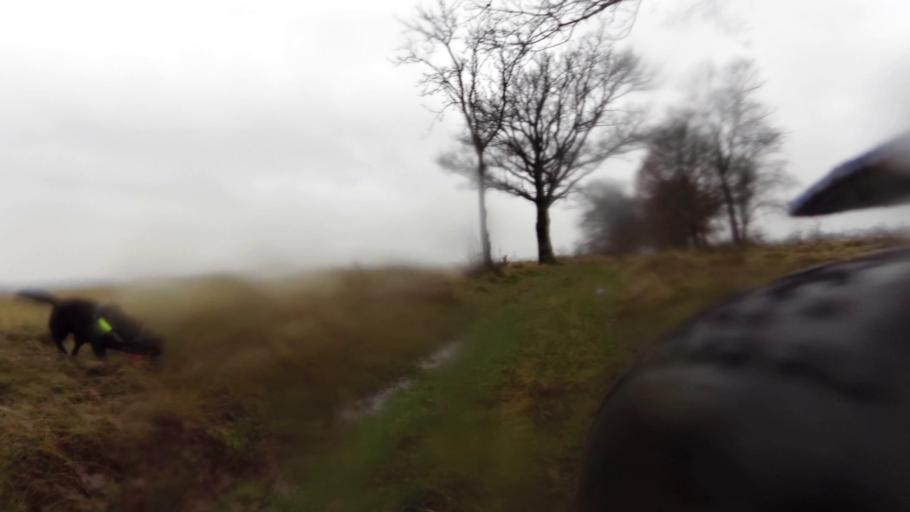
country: PL
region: West Pomeranian Voivodeship
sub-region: Powiat drawski
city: Drawsko Pomorskie
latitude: 53.5538
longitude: 15.8345
